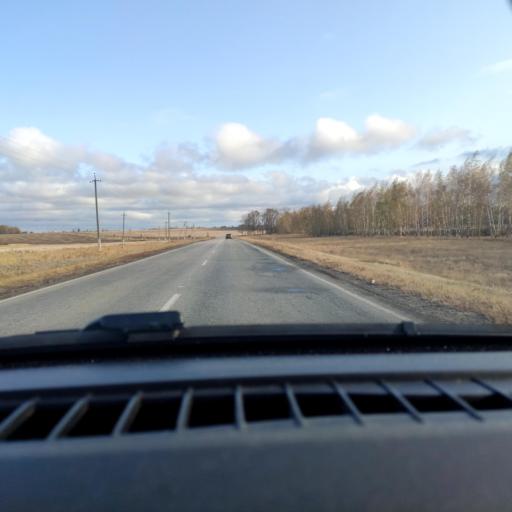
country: RU
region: Belgorod
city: Ilovka
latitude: 50.7157
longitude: 38.6698
